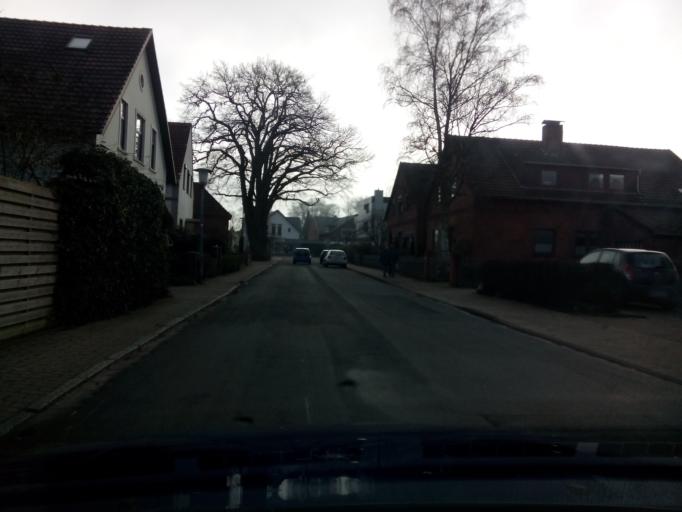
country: DE
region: Lower Saxony
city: Lilienthal
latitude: 53.1416
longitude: 8.9058
